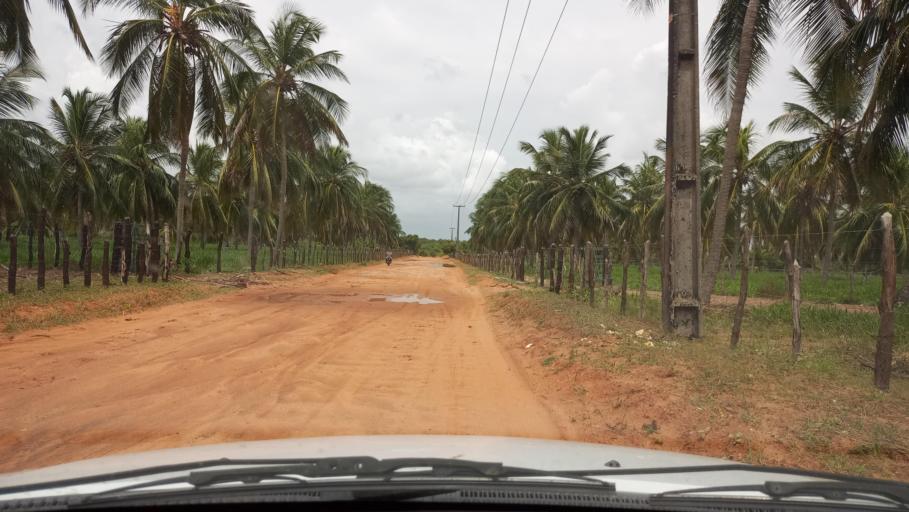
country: BR
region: Rio Grande do Norte
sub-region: Maxaranguape
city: Sao Miguel
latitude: -5.4836
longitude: -35.3146
